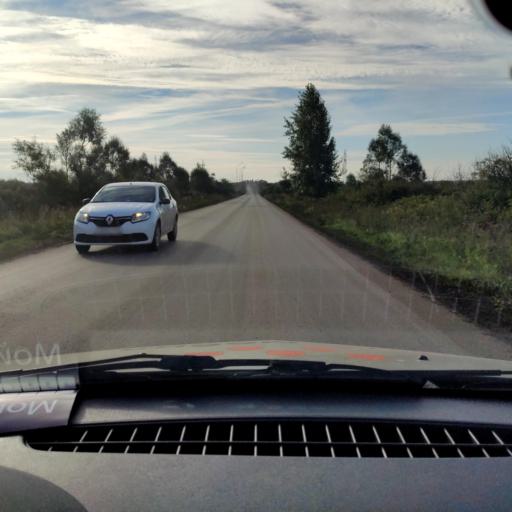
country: RU
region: Bashkortostan
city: Kabakovo
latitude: 54.6713
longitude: 56.1475
